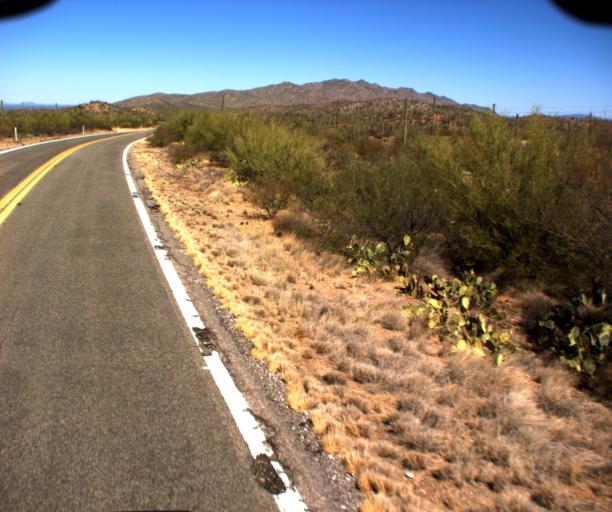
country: US
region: Arizona
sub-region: Pima County
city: Sells
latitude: 32.1757
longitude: -112.1880
